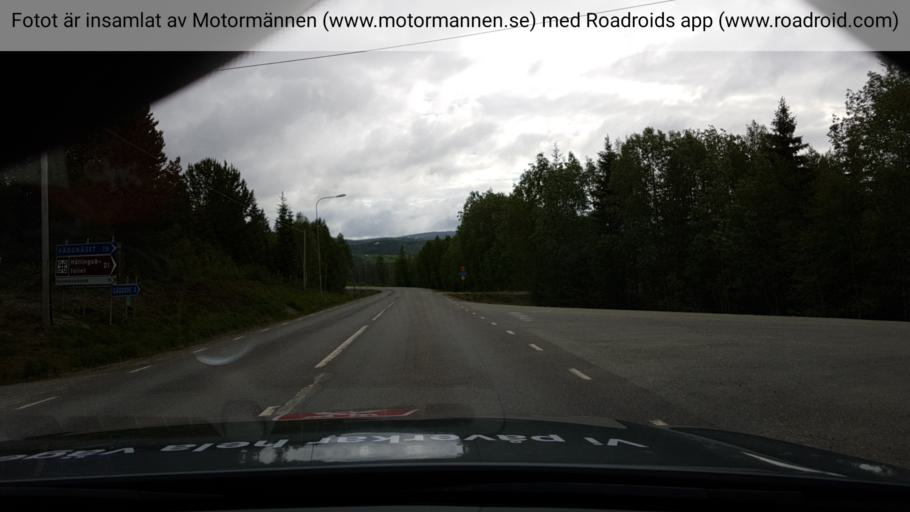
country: NO
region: Nord-Trondelag
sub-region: Lierne
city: Sandvika
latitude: 64.4814
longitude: 14.1258
